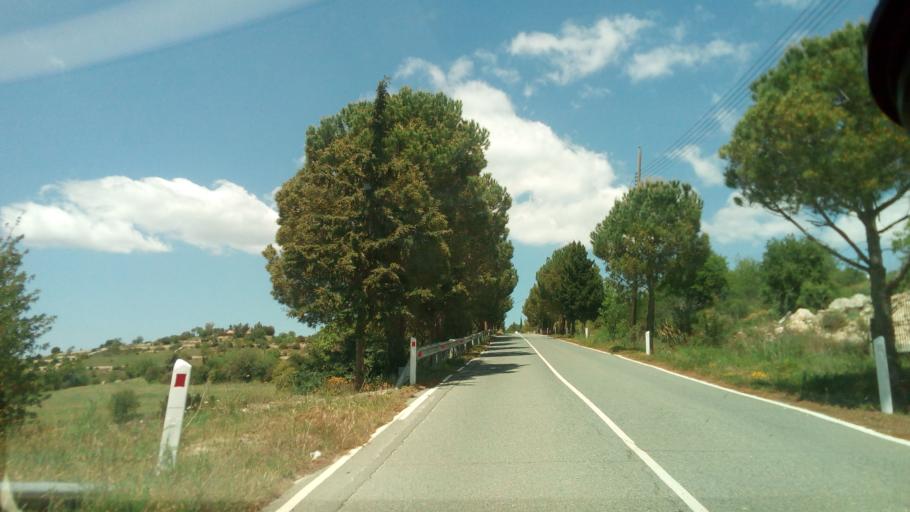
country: CY
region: Limassol
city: Pachna
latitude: 34.8333
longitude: 32.7723
